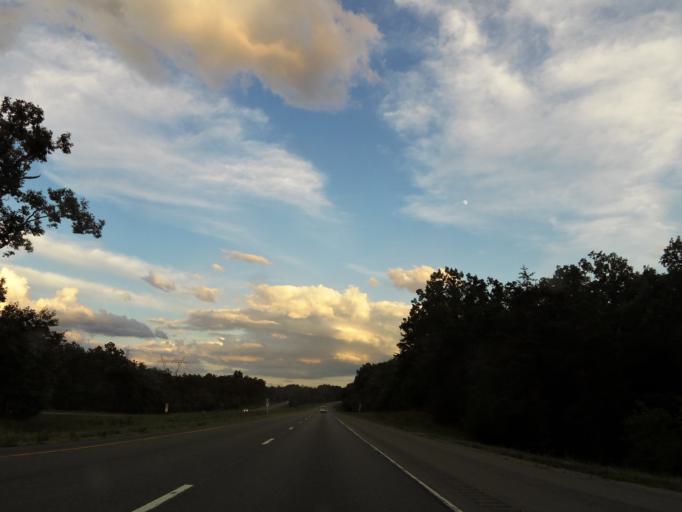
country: US
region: Tennessee
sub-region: Cumberland County
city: Crossville
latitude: 36.0413
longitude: -85.1130
